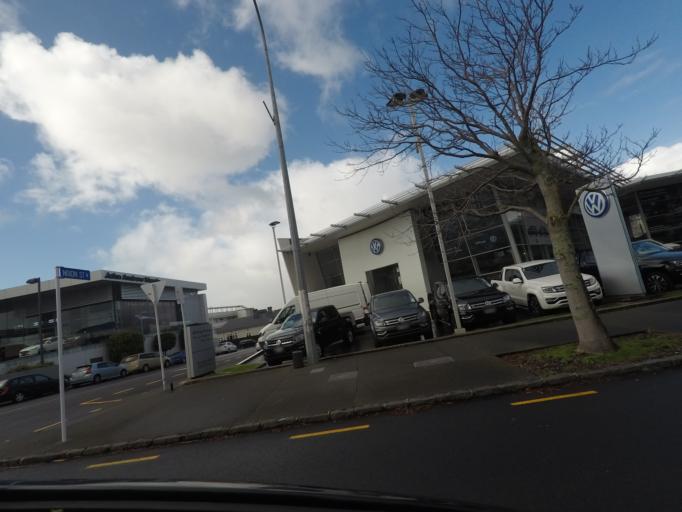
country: NZ
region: Auckland
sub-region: Auckland
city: Auckland
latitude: -36.8609
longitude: 174.7514
